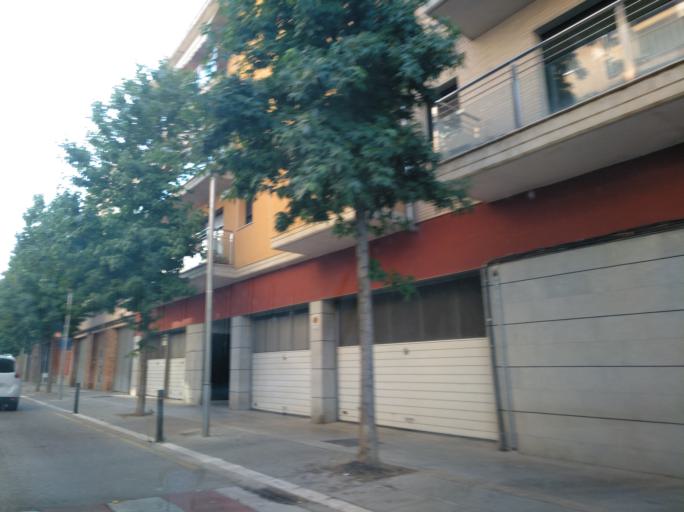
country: ES
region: Catalonia
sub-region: Provincia de Girona
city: Salt
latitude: 41.9723
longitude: 2.7841
